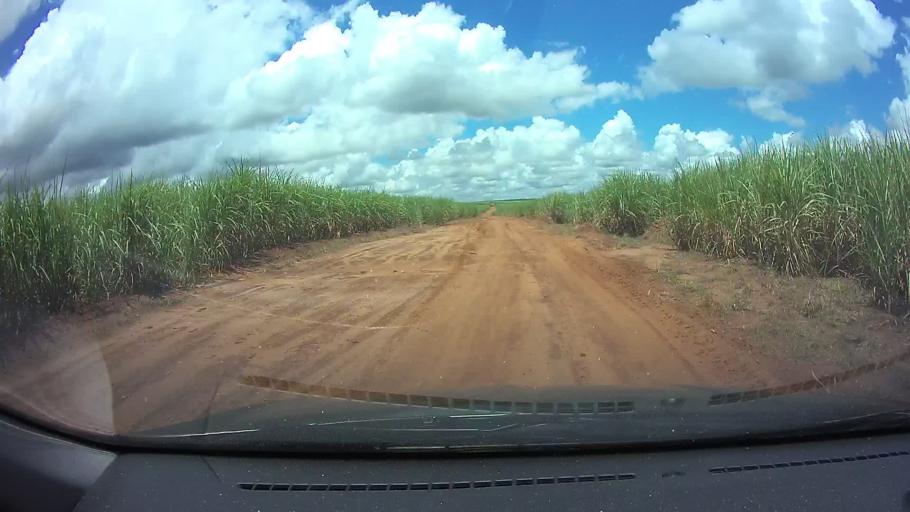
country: PY
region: Paraguari
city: La Colmena
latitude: -25.9542
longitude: -56.7664
